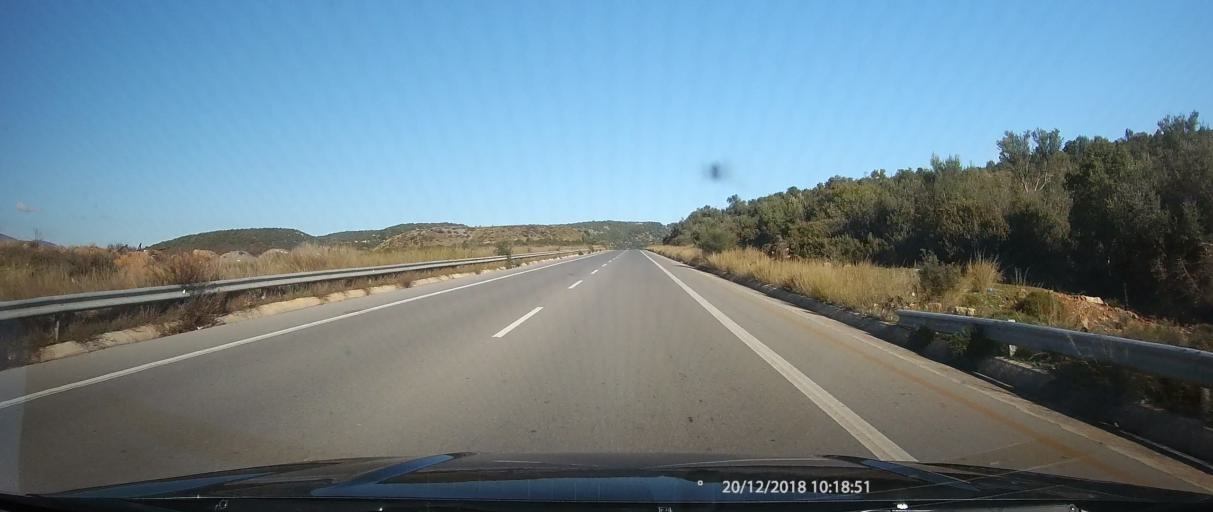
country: GR
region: Peloponnese
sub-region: Nomos Lakonias
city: Magoula
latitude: 37.1238
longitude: 22.4204
